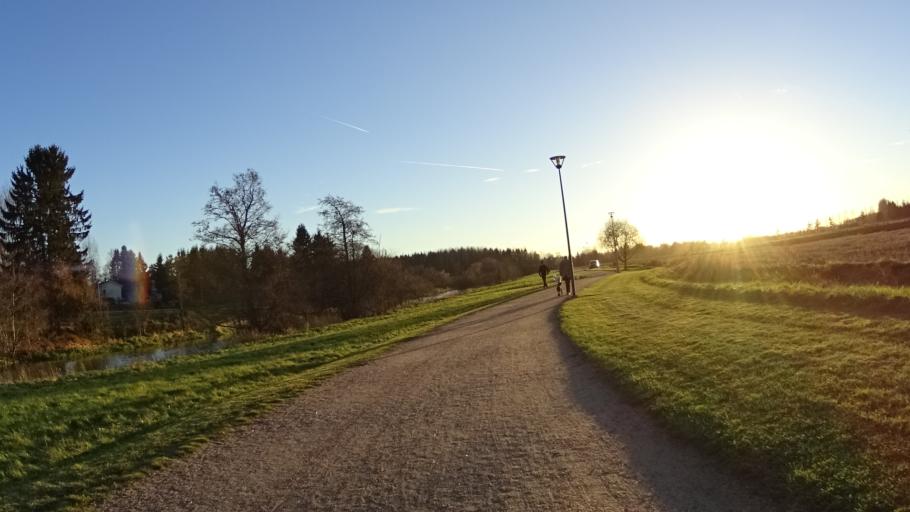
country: FI
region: Uusimaa
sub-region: Helsinki
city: Vantaa
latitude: 60.2845
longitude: 24.9987
